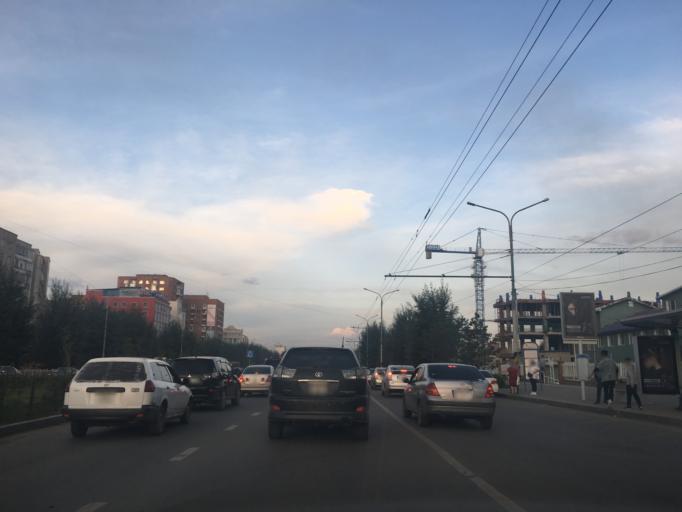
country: MN
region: Ulaanbaatar
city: Ulaanbaatar
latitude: 47.9122
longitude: 106.8471
